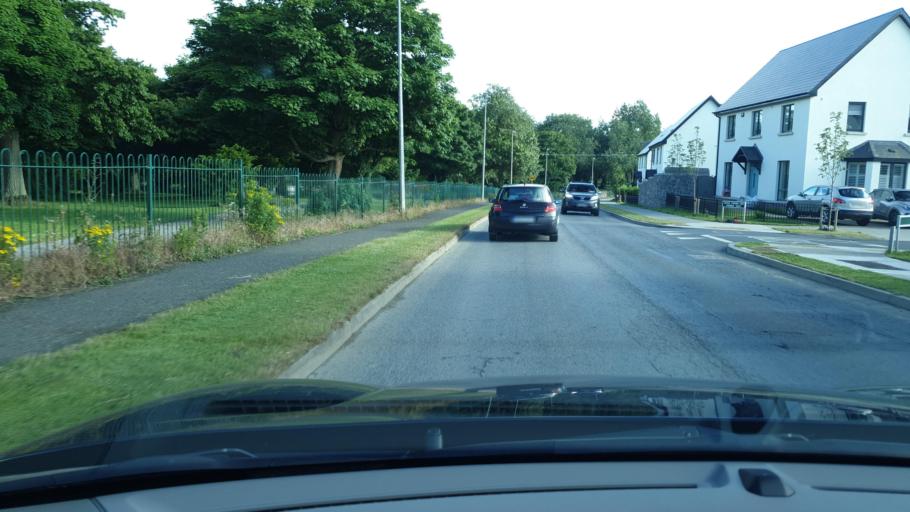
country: IE
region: Leinster
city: An Ros
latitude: 53.5260
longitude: -6.0977
